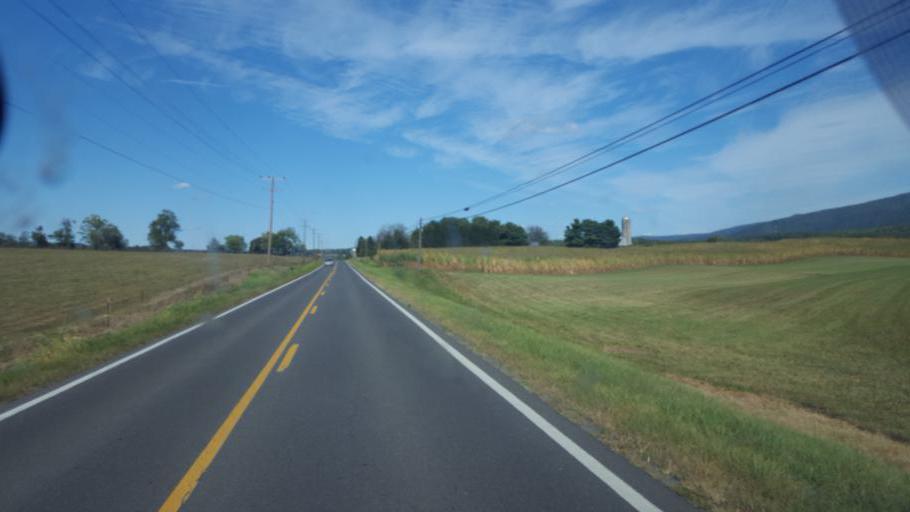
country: US
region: Virginia
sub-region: Page County
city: Luray
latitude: 38.7144
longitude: -78.4308
